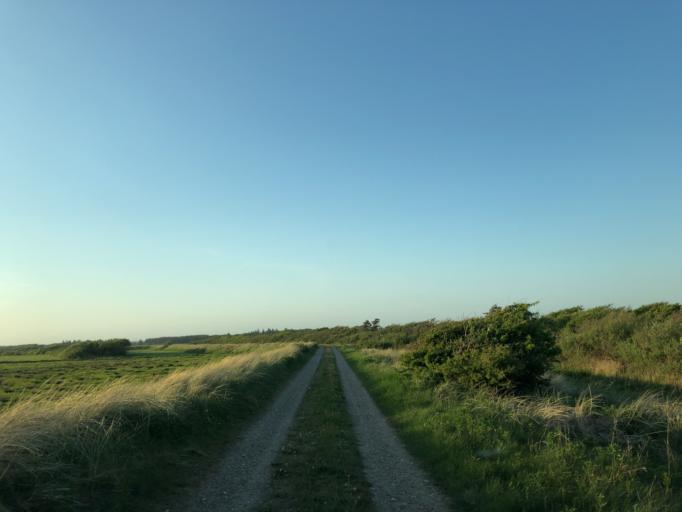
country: DK
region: Central Jutland
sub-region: Holstebro Kommune
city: Ulfborg
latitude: 56.2436
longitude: 8.1631
